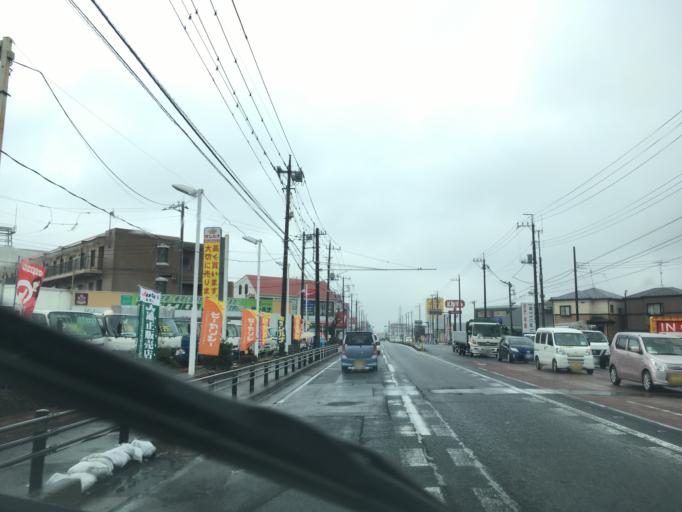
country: JP
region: Saitama
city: Koshigaya
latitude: 35.8898
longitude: 139.7714
